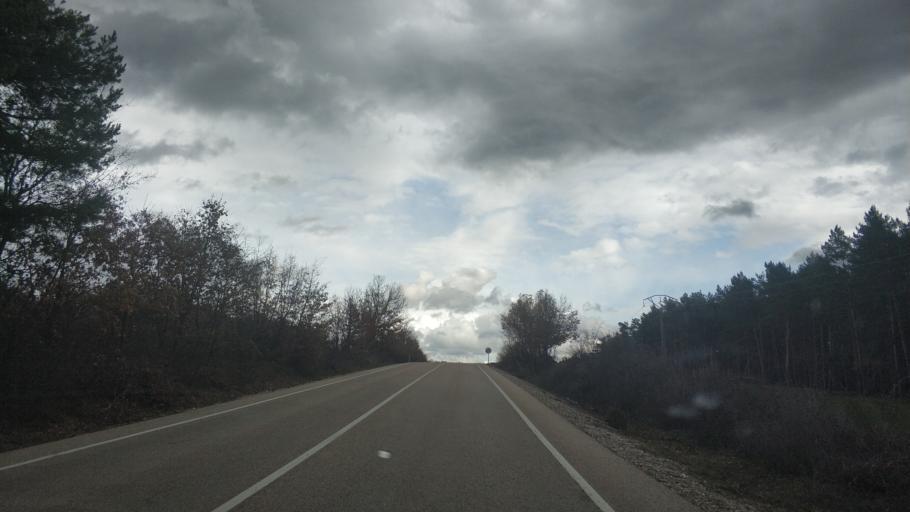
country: ES
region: Castille and Leon
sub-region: Provincia de Burgos
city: Quintanar de la Sierra
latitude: 41.9691
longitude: -3.0355
